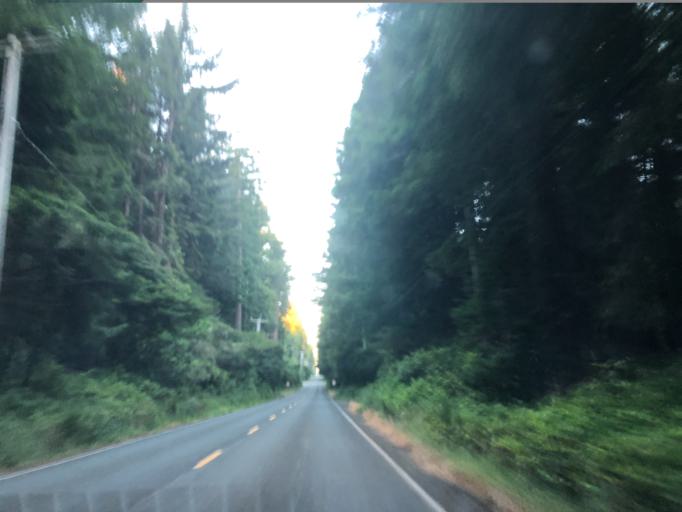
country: US
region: California
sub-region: Humboldt County
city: Westhaven-Moonstone
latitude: 41.0853
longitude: -124.1490
